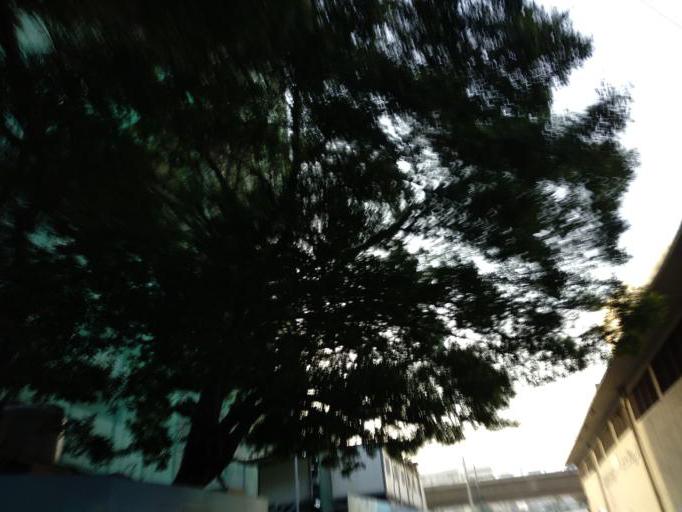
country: LB
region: Beyrouth
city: Beirut
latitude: 33.8810
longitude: 35.5302
